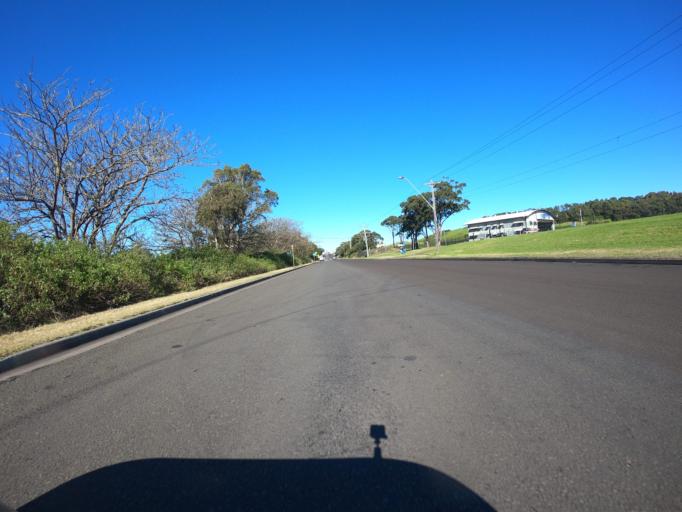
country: AU
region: New South Wales
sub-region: Wollongong
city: Wollongong
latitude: -34.4394
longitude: 150.8971
